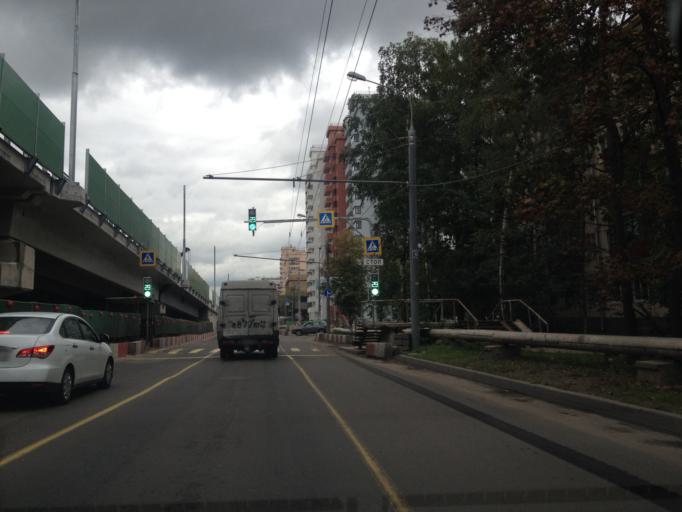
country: RU
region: Moscow
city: Gol'yanovo
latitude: 55.8102
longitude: 37.8036
